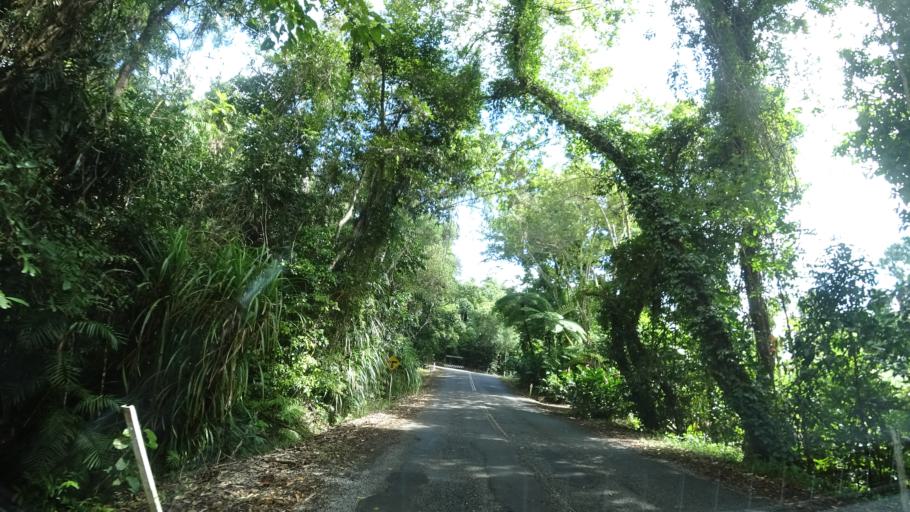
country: AU
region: Queensland
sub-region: Cairns
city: Port Douglas
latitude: -16.2375
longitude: 145.4258
